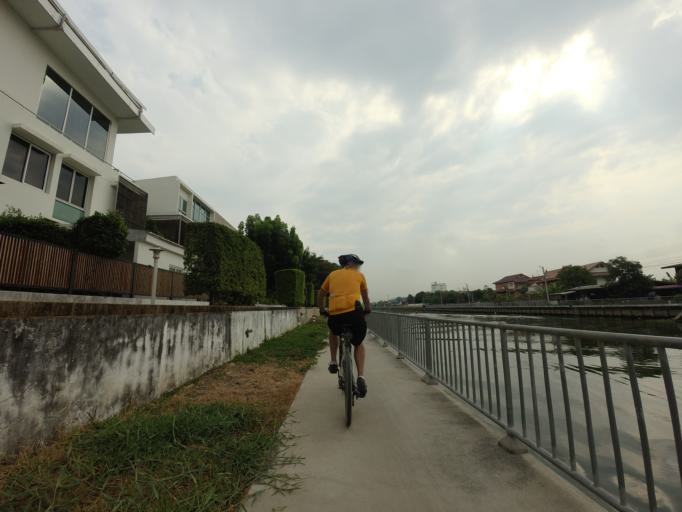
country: TH
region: Bangkok
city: Suan Luang
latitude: 13.7213
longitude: 100.6627
